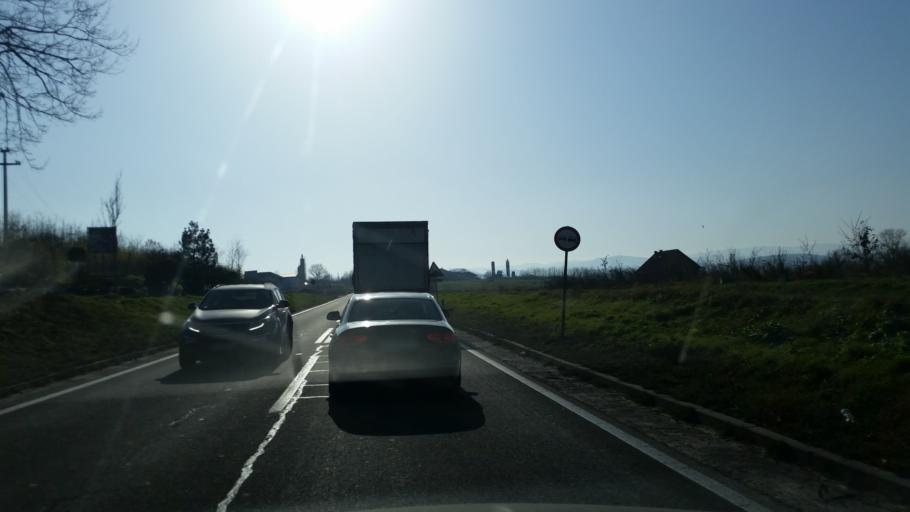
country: RS
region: Central Serbia
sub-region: Kolubarski Okrug
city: Ljig
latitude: 44.2664
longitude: 20.2850
